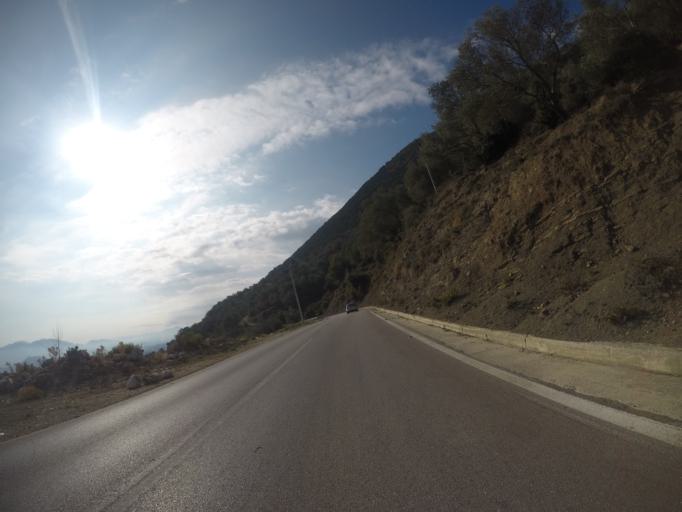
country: AL
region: Vlore
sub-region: Rrethi i Sarandes
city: Lukove
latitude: 39.9542
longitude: 19.9643
